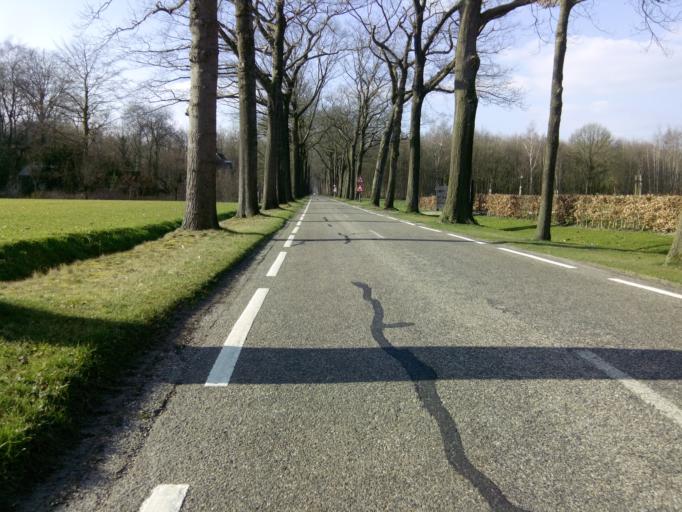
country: NL
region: Utrecht
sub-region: Gemeente Leusden
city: Leusden
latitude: 52.0984
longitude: 5.4714
